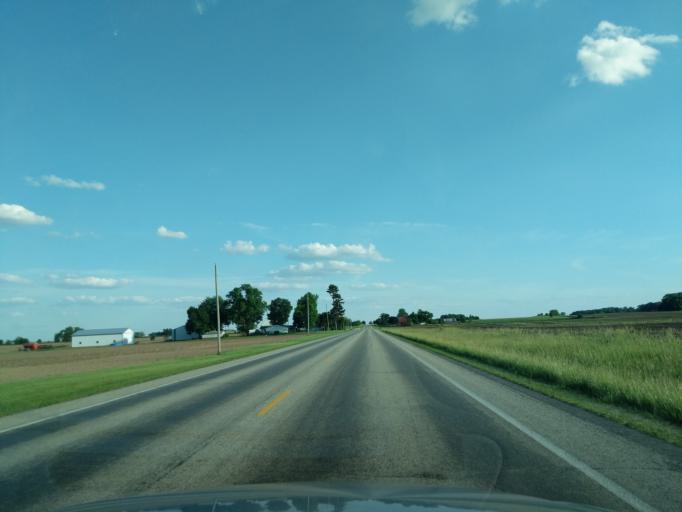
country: US
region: Indiana
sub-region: Huntington County
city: Roanoke
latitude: 40.9892
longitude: -85.4716
